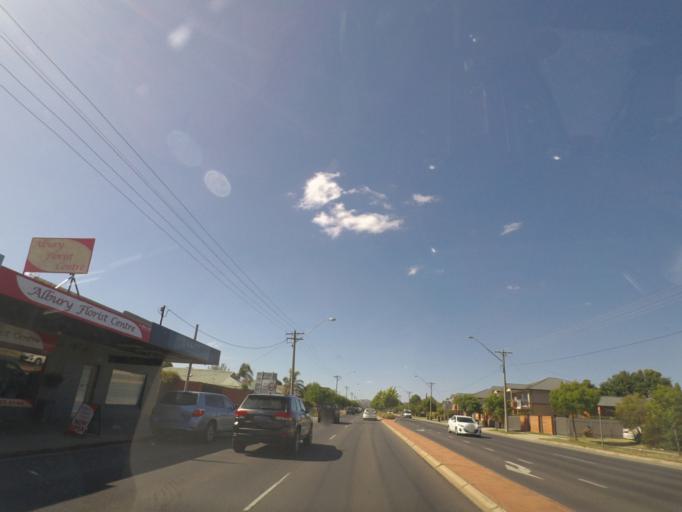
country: AU
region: New South Wales
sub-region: Albury Municipality
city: North Albury
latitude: -36.0627
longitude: 146.9316
